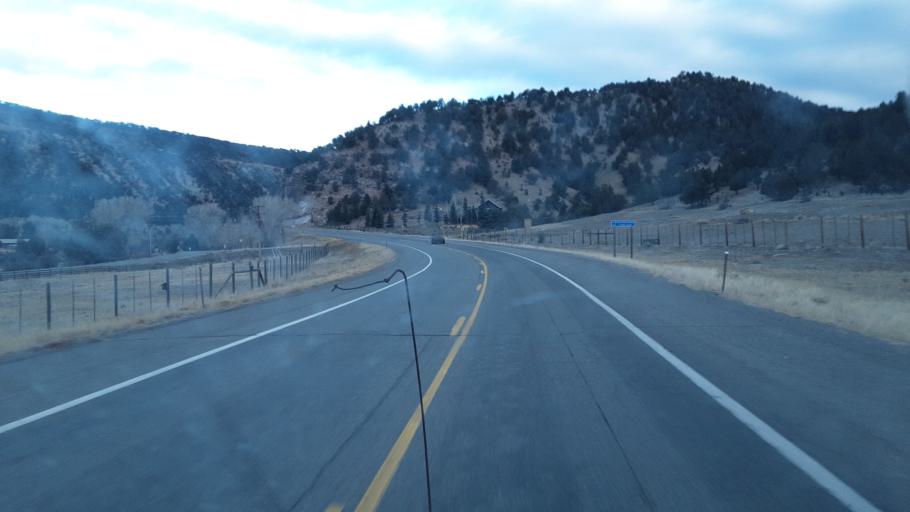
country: US
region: Colorado
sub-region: Ouray County
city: Ouray
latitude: 38.1817
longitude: -107.7439
